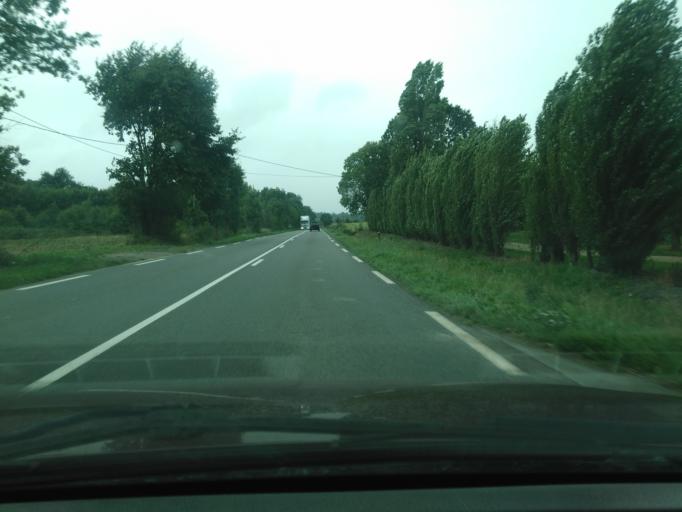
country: FR
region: Pays de la Loire
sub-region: Departement de la Vendee
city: Sainte-Hermine
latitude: 46.5787
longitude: -1.1078
